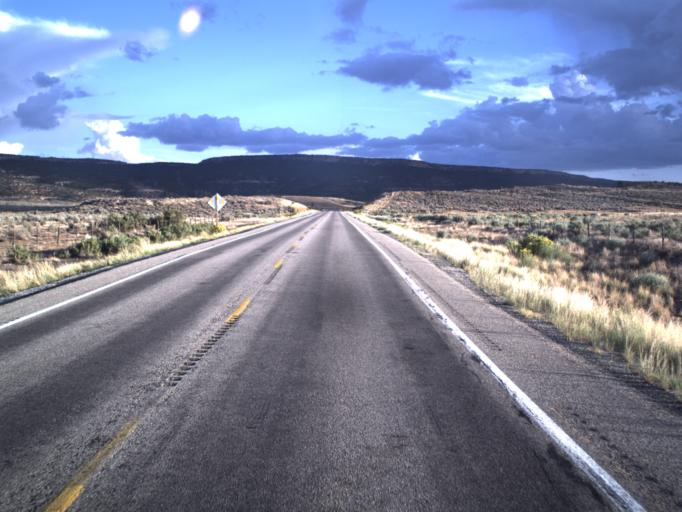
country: US
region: Utah
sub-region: San Juan County
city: Monticello
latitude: 38.0647
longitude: -109.3465
